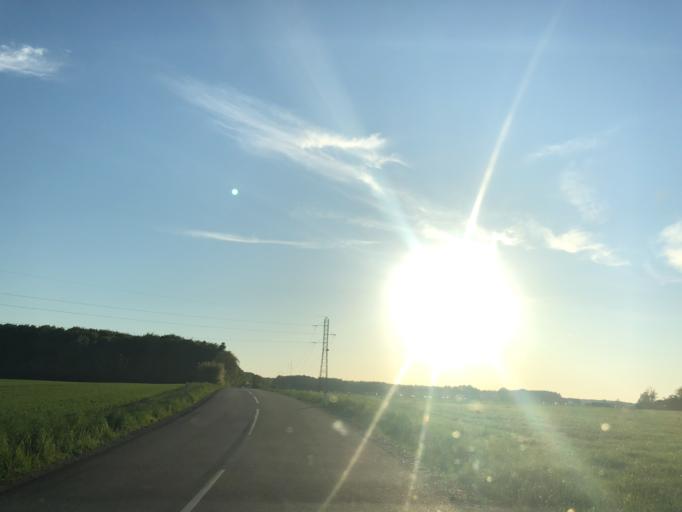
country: DK
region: Zealand
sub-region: Koge Kommune
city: Ejby
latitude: 55.4181
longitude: 12.1130
